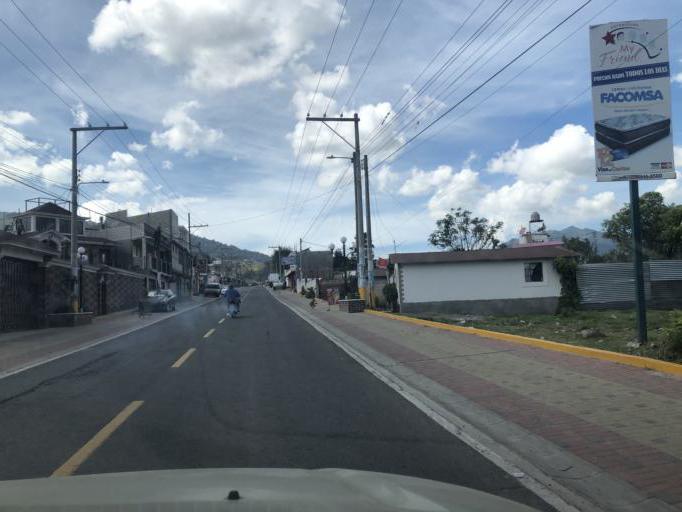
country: GT
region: Quetzaltenango
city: San Mateo
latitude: 14.8621
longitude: -91.5854
